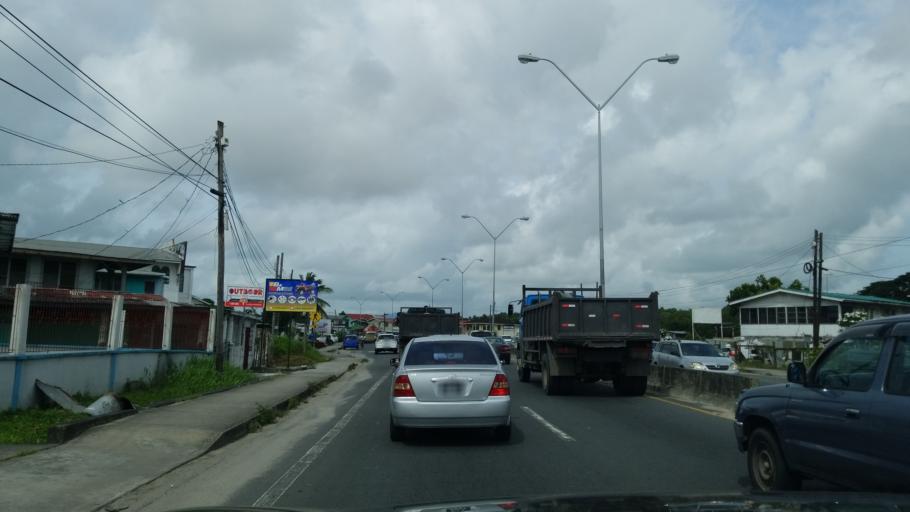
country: GY
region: Demerara-Mahaica
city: Georgetown
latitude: 6.7713
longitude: -58.1749
